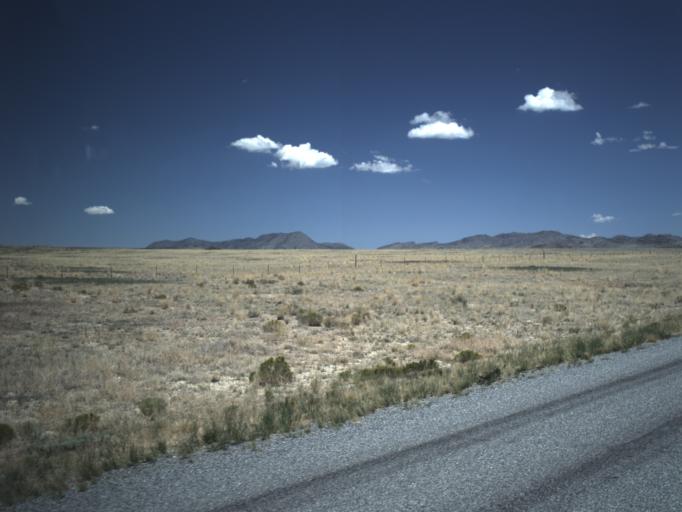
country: US
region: Utah
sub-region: Beaver County
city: Milford
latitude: 39.0432
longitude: -113.8046
